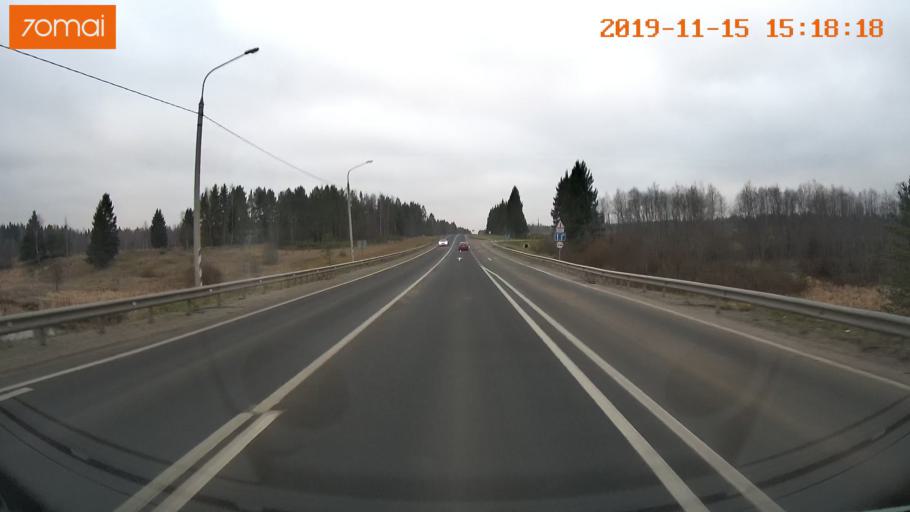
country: RU
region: Jaroslavl
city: Danilov
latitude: 58.2494
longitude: 40.1809
